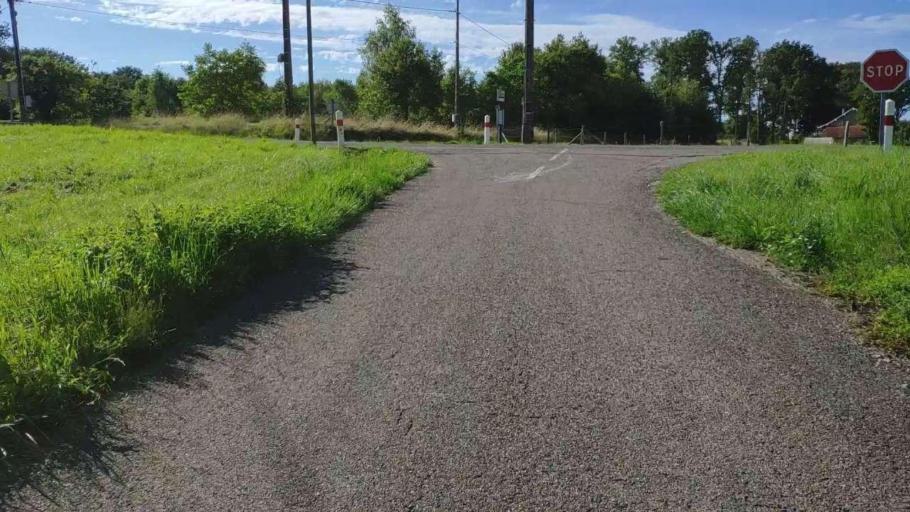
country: FR
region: Franche-Comte
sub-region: Departement du Jura
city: Bletterans
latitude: 46.8264
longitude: 5.5014
